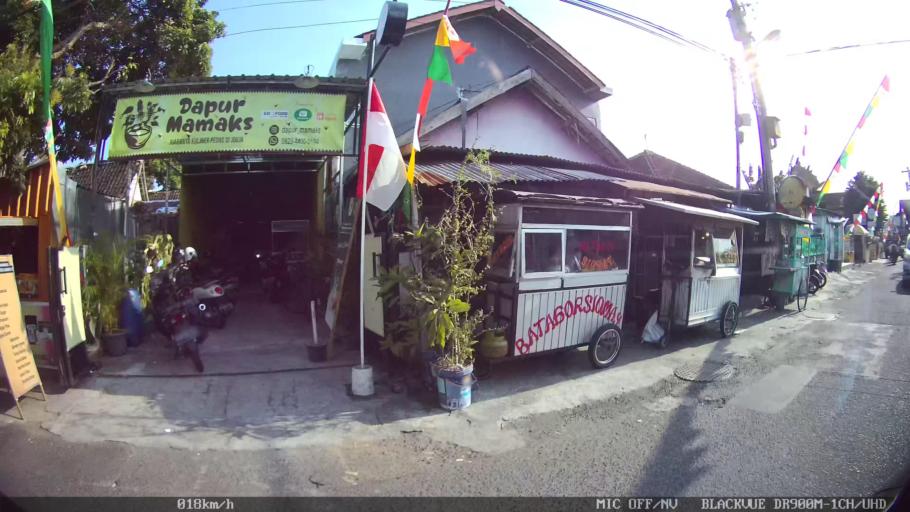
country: ID
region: Daerah Istimewa Yogyakarta
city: Yogyakarta
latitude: -7.7922
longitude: 110.3506
